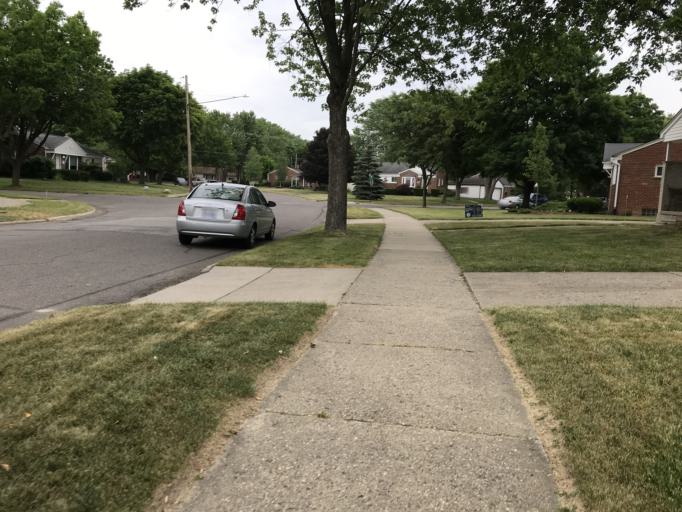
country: US
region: Michigan
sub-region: Oakland County
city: Farmington
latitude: 42.4666
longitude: -83.3620
